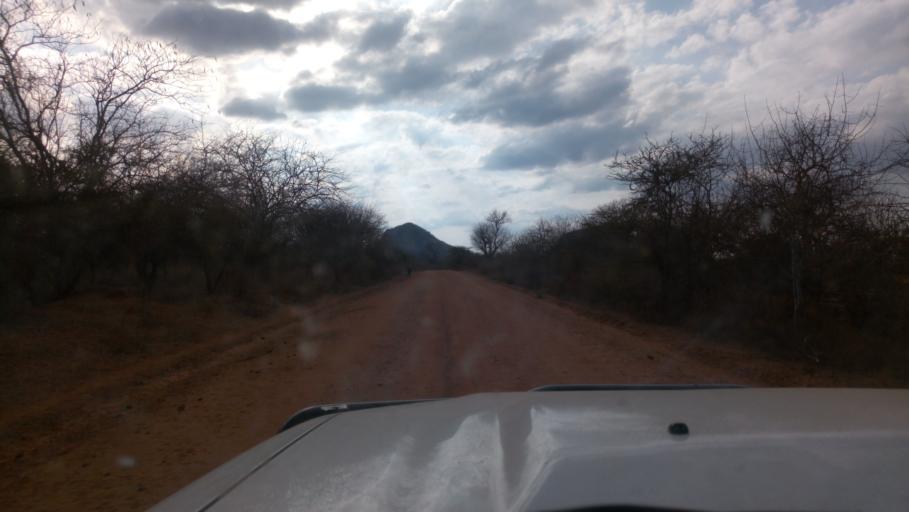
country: KE
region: Kitui
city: Kitui
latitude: -1.7174
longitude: 38.3791
